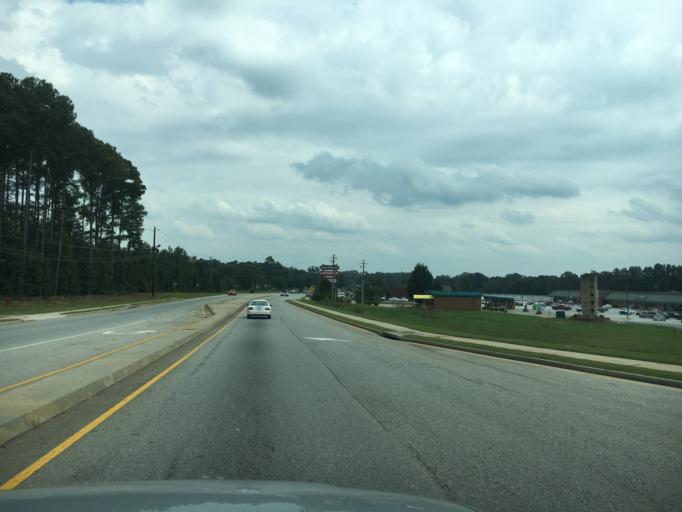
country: US
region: Georgia
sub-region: Franklin County
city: Lavonia
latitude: 34.4443
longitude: -83.1161
